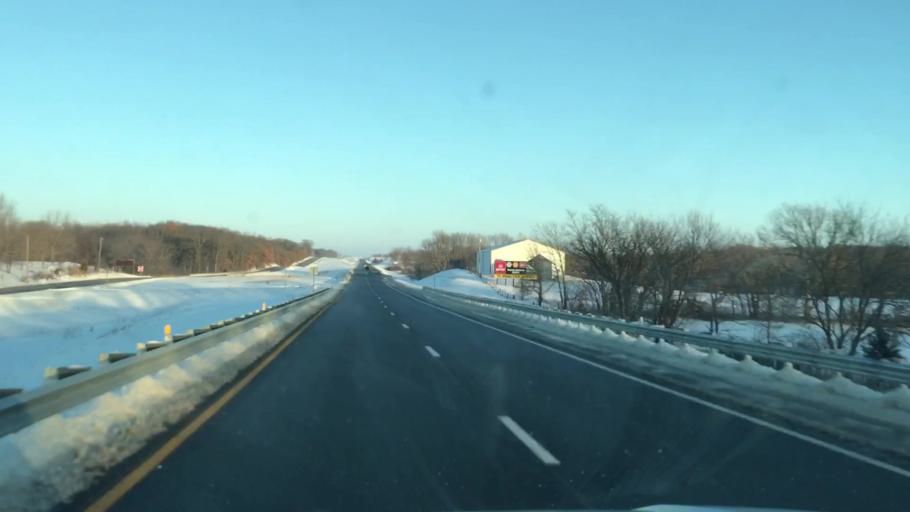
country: US
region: Missouri
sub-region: DeKalb County
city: Maysville
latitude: 39.7620
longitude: -94.4862
